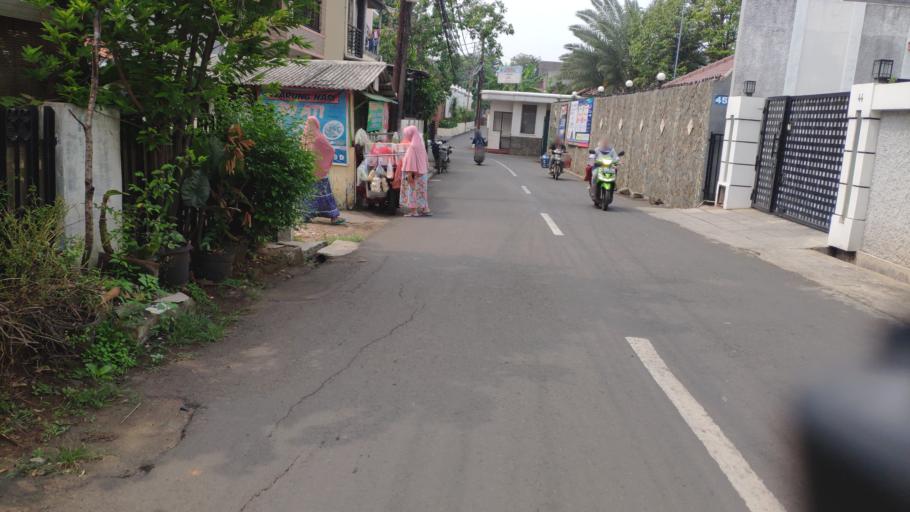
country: ID
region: West Java
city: Depok
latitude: -6.3225
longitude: 106.8214
